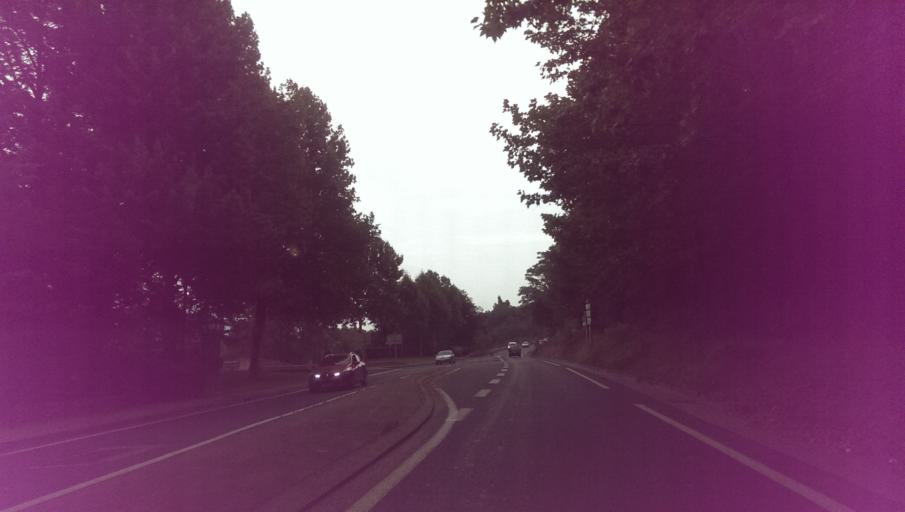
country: FR
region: Languedoc-Roussillon
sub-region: Departement des Pyrenees-Orientales
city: Ria-Sirach
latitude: 42.6080
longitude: 2.4037
